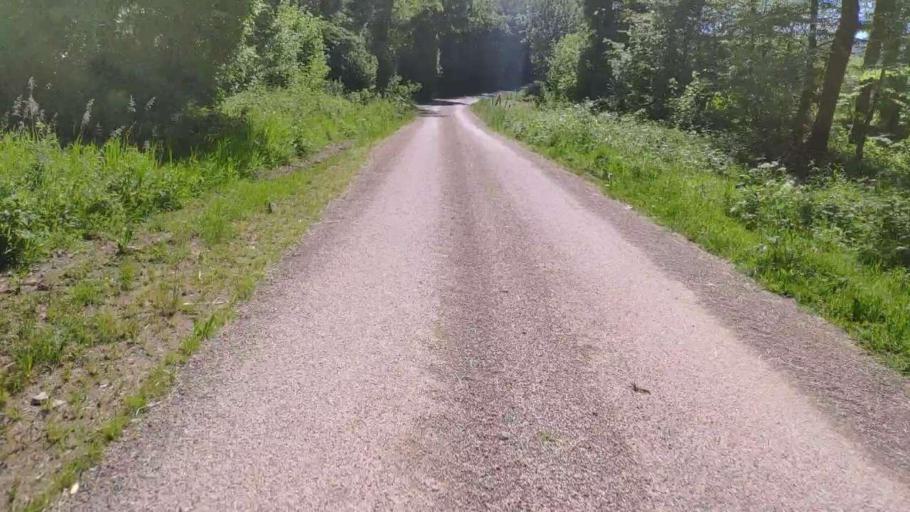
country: FR
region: Franche-Comte
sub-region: Departement du Jura
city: Clairvaux-les-Lacs
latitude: 46.7001
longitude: 5.7140
